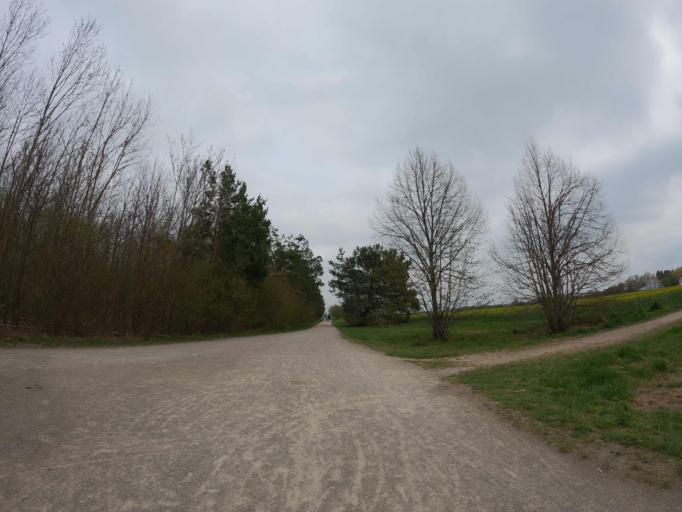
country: DE
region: Bavaria
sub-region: Upper Bavaria
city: Feldkirchen
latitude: 48.1332
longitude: 11.7162
